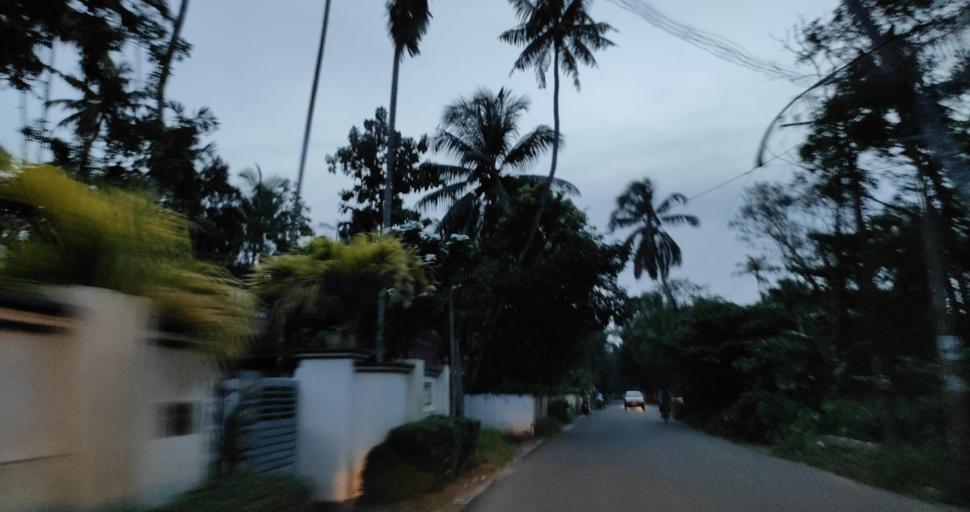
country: IN
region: Kerala
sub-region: Alappuzha
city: Vayalar
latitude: 9.7040
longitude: 76.3106
